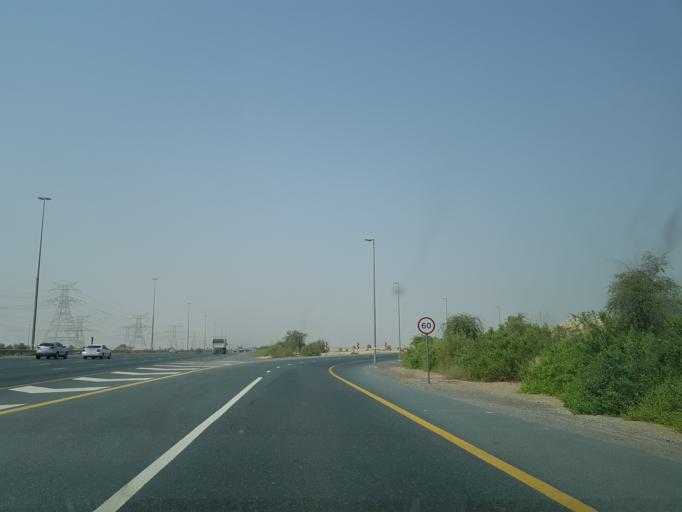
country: AE
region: Dubai
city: Dubai
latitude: 25.0519
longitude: 55.3111
